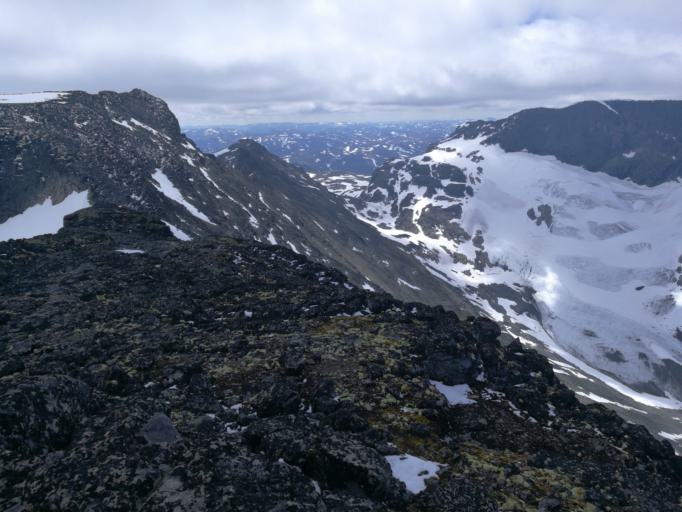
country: NO
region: Oppland
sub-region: Vang
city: Vang
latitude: 61.4218
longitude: 8.5089
